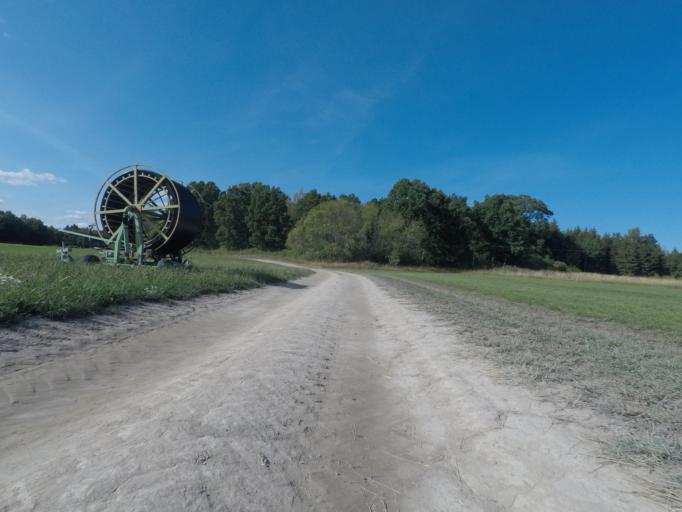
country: SE
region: Soedermanland
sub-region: Eskilstuna Kommun
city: Kvicksund
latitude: 59.4403
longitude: 16.2777
